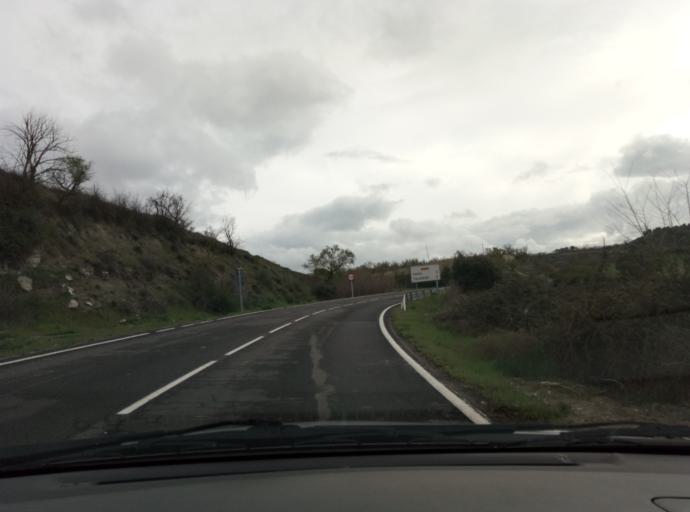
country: ES
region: Catalonia
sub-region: Provincia de Lleida
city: Cervera
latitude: 41.6241
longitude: 1.3398
